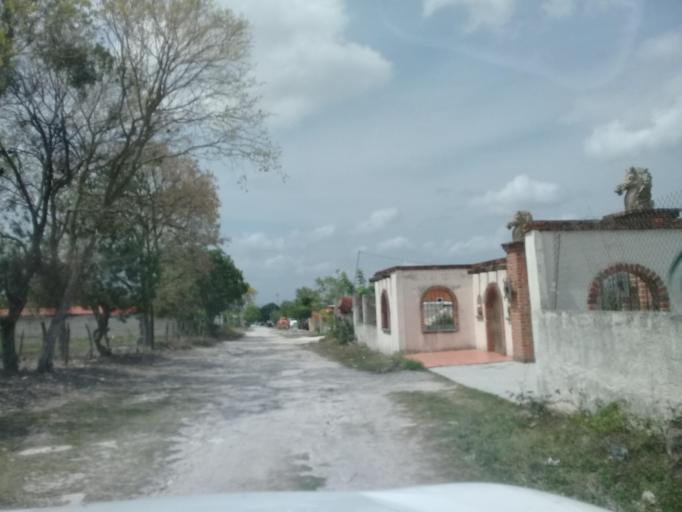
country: MX
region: Veracruz
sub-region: Emiliano Zapata
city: Plan del Rio
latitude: 19.3556
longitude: -96.6608
